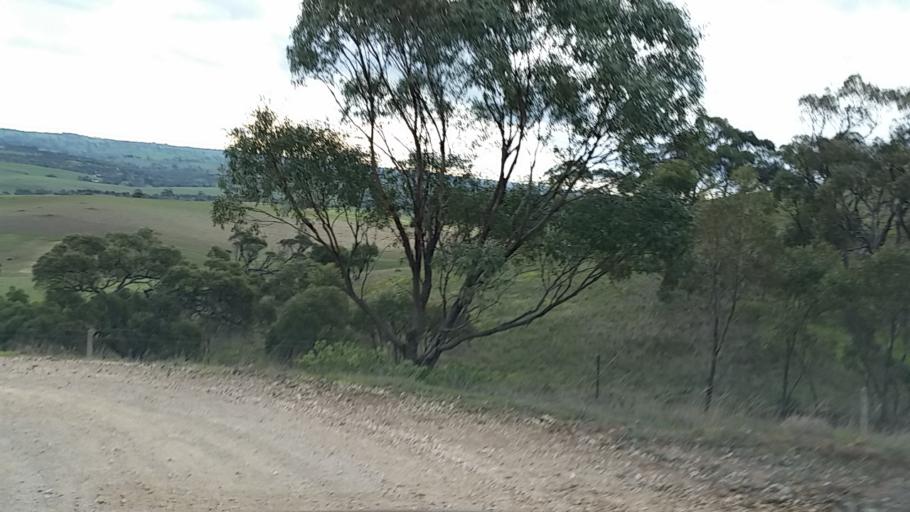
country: AU
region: South Australia
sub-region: Mount Barker
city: Callington
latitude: -34.9989
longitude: 139.0521
